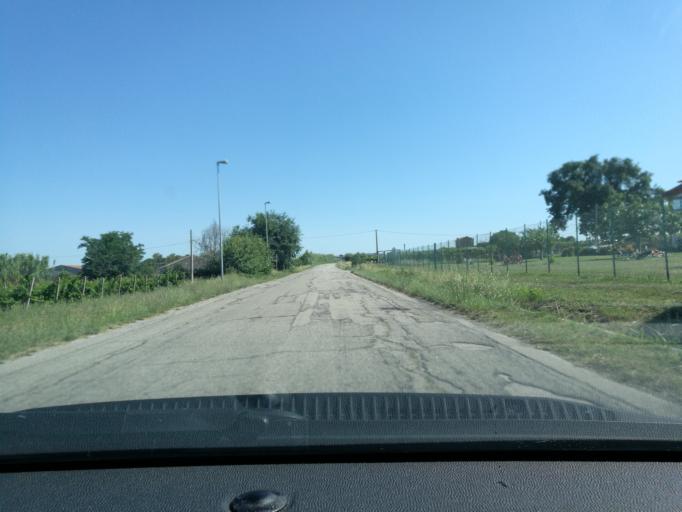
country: IT
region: Abruzzo
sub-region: Provincia di Chieti
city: Vasto
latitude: 42.1630
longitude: 14.7030
